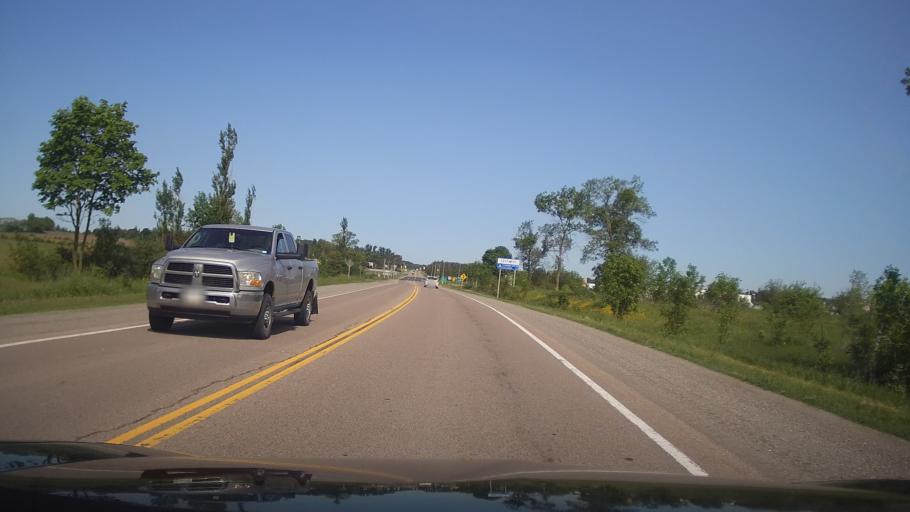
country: CA
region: Ontario
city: Omemee
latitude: 44.3447
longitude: -78.7699
